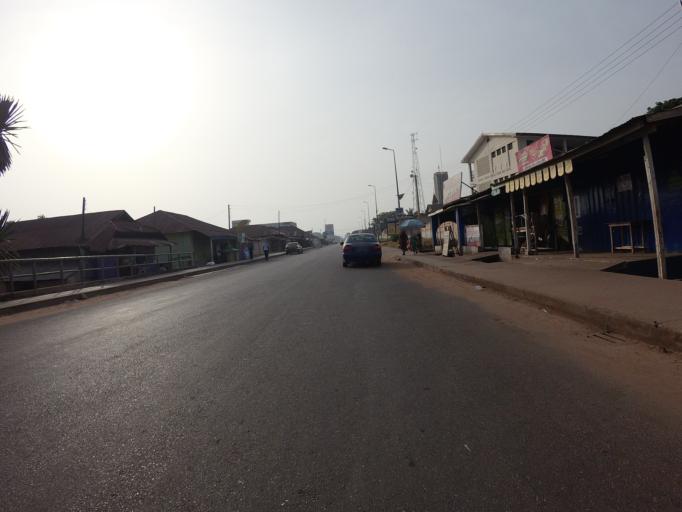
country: GH
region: Volta
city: Ho
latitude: 6.6133
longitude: 0.4695
